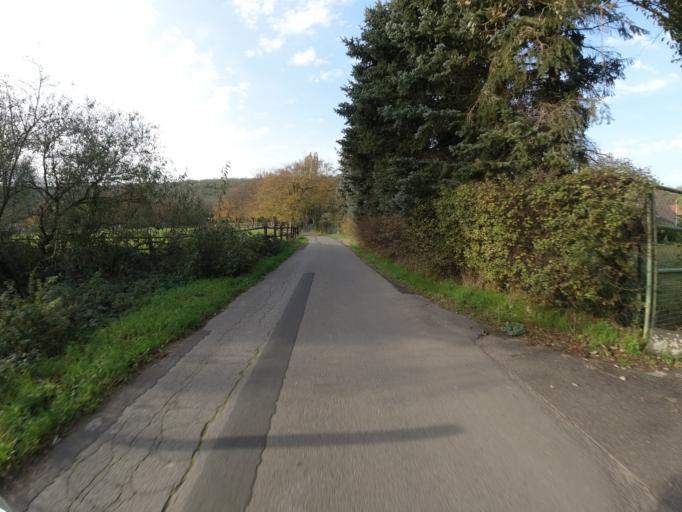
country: DE
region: North Rhine-Westphalia
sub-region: Regierungsbezirk Dusseldorf
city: Kamp-Lintfort
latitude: 51.4707
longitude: 6.5764
